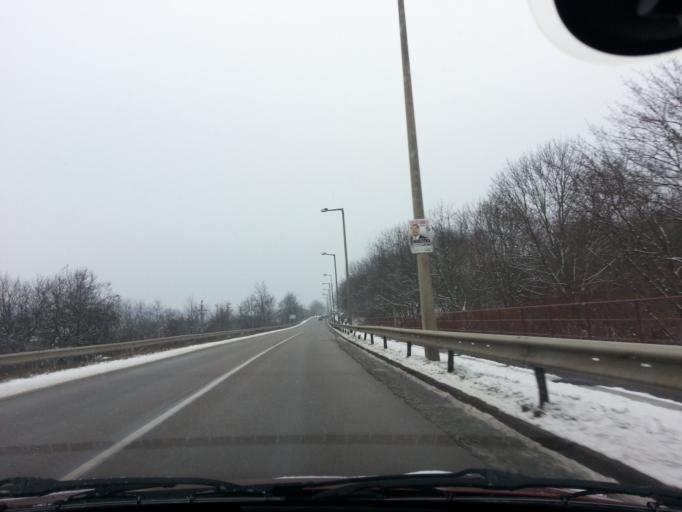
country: HU
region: Nograd
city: Salgotarjan
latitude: 48.0797
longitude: 19.7870
